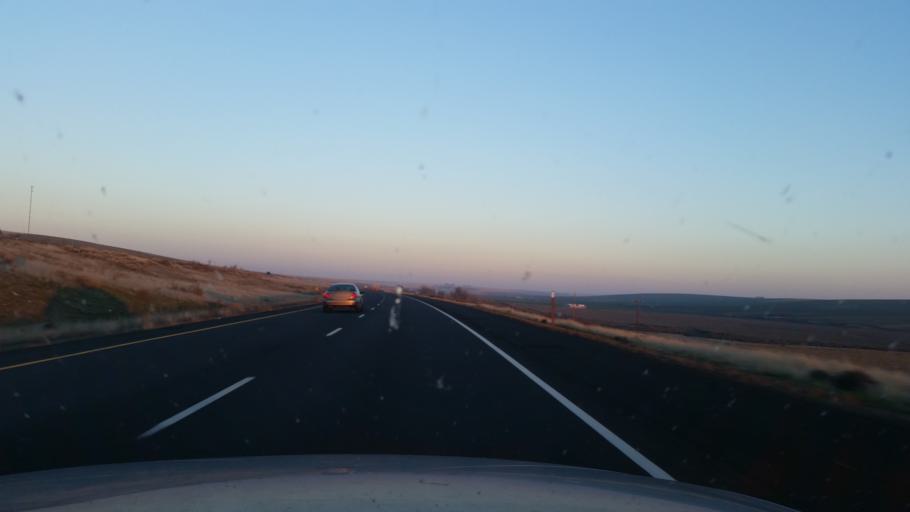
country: US
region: Washington
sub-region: Grant County
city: Warden
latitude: 47.0842
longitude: -118.9544
